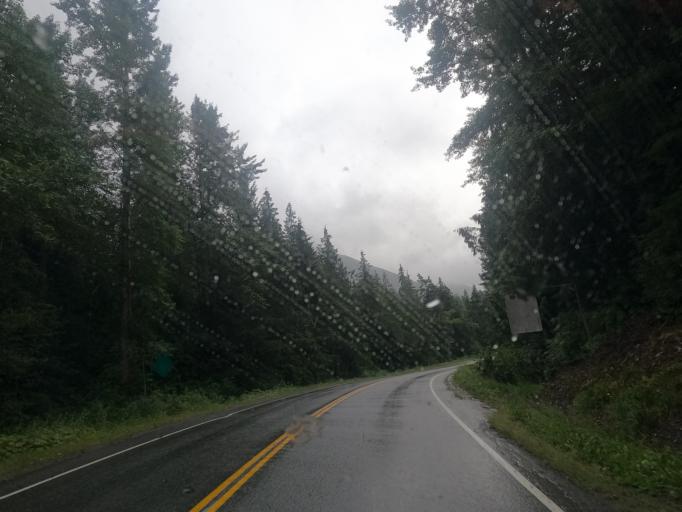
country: CA
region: British Columbia
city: Lillooet
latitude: 50.5307
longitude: -122.1560
